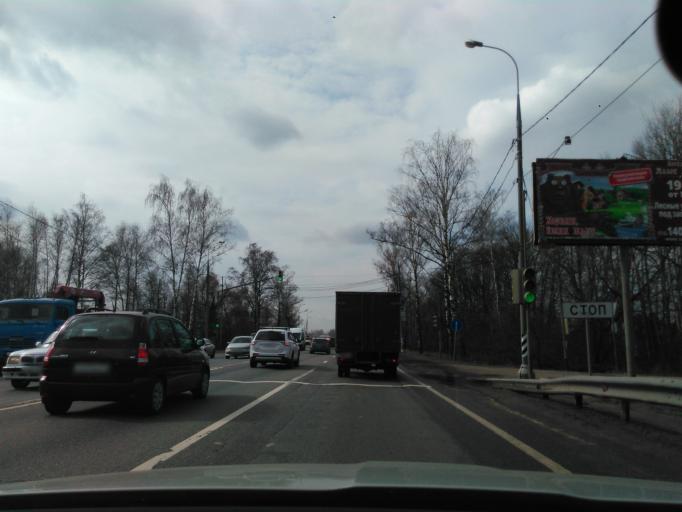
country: RU
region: Moskovskaya
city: Sheremet'yevskiy
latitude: 55.9823
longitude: 37.5273
